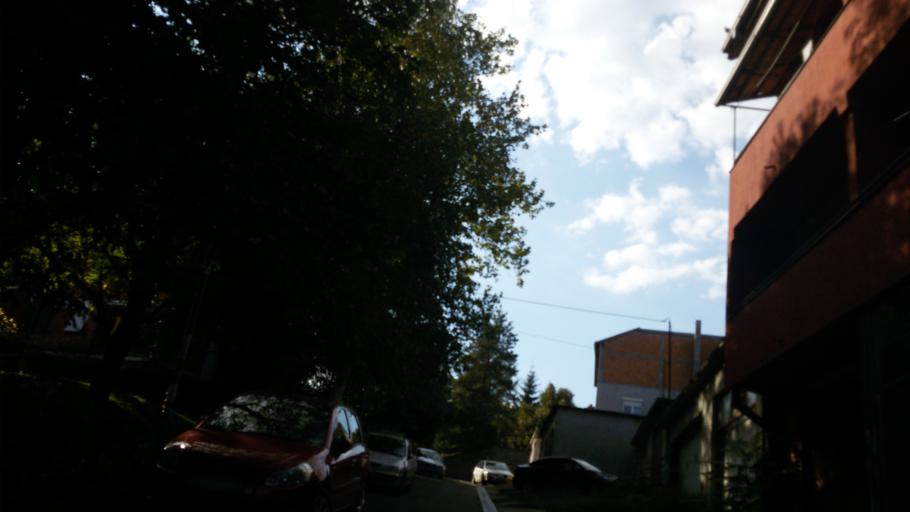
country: RS
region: Central Serbia
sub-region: Belgrade
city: Rakovica
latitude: 44.7368
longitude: 20.4276
